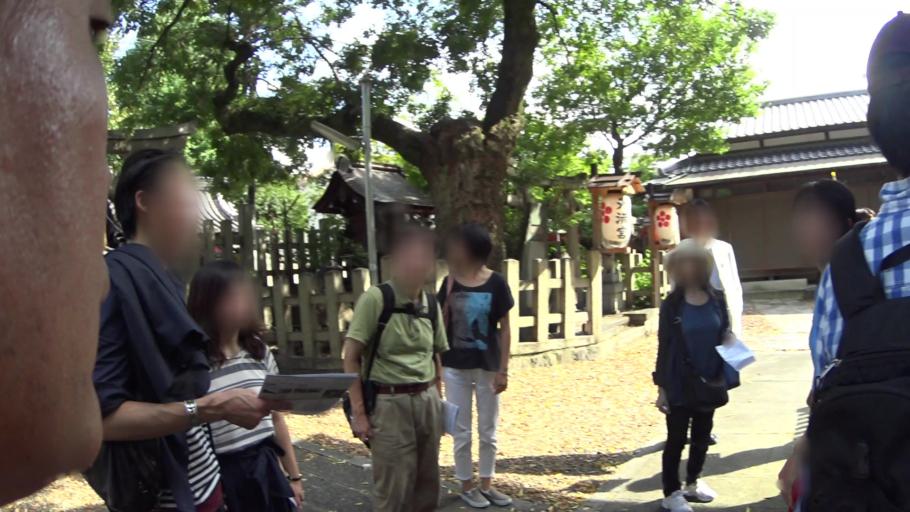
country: JP
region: Kyoto
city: Kyoto
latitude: 35.0093
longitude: 135.7768
